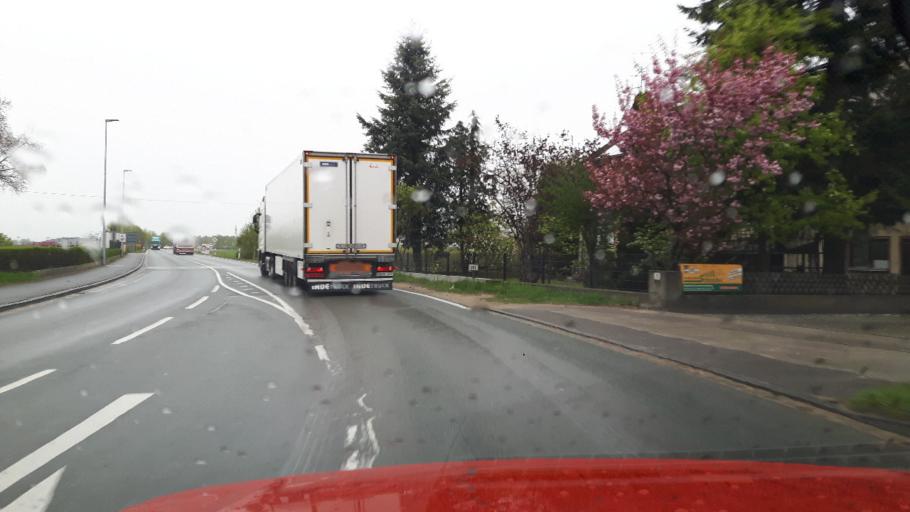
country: DE
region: Bavaria
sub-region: Regierungsbezirk Mittelfranken
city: Merkendorf
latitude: 49.1999
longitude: 10.6991
